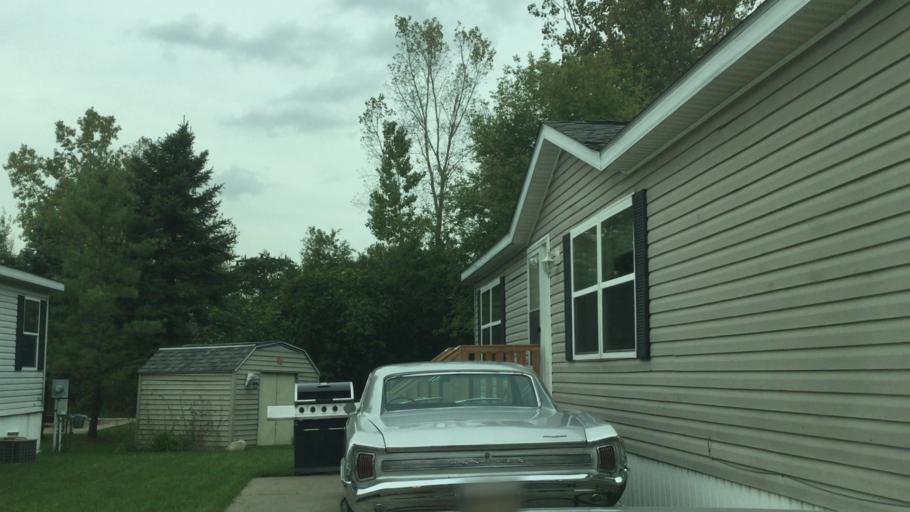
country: US
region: Michigan
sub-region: Oakland County
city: Waterford
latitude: 42.6609
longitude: -83.4710
